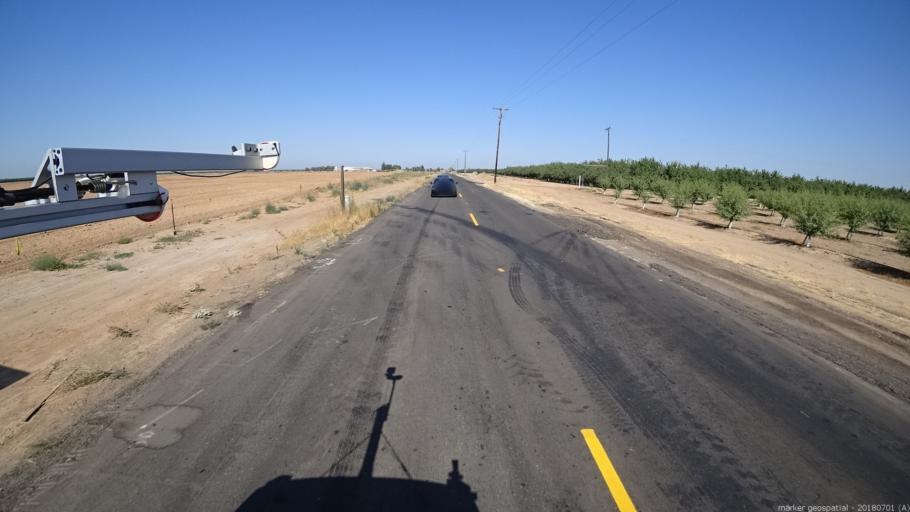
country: US
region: California
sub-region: Madera County
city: Parksdale
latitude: 36.8803
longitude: -119.9600
